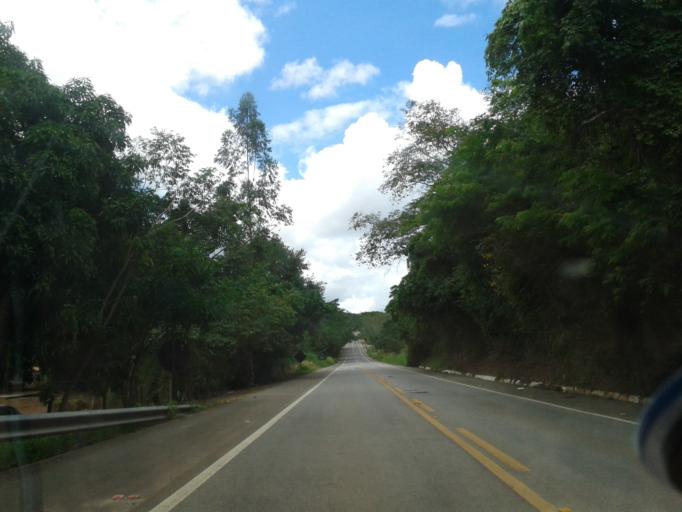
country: BR
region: Goias
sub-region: Goias
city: Goias
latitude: -15.9178
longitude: -50.1279
